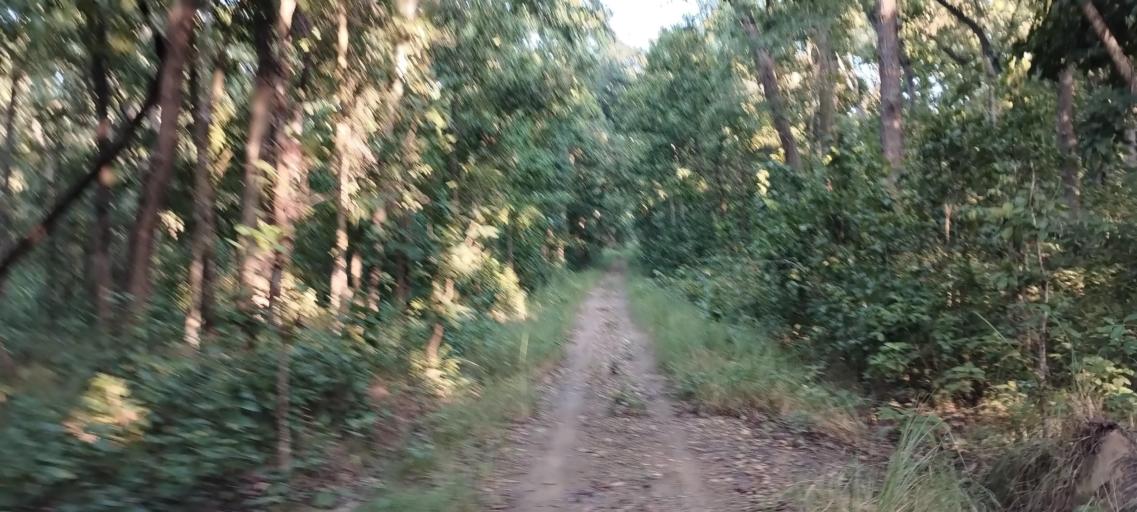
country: NP
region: Far Western
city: Tikapur
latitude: 28.4868
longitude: 81.2617
